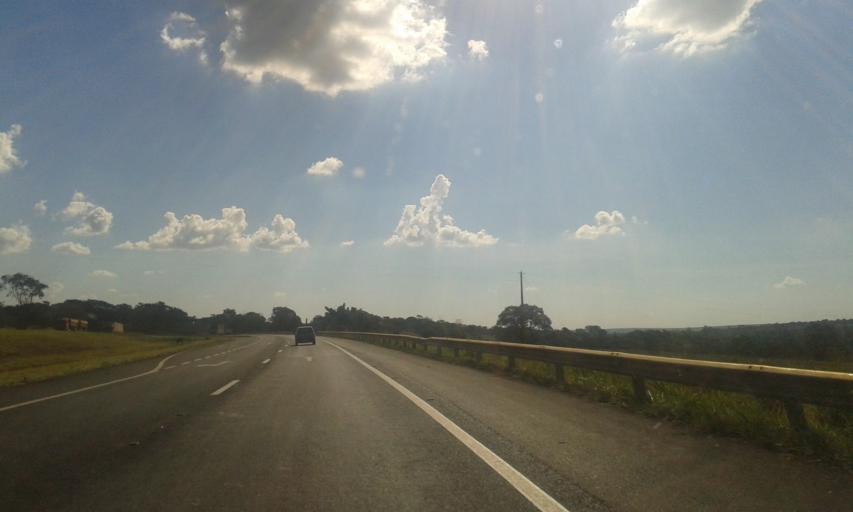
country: BR
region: Minas Gerais
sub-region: Monte Alegre De Minas
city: Monte Alegre de Minas
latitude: -18.8934
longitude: -48.6606
